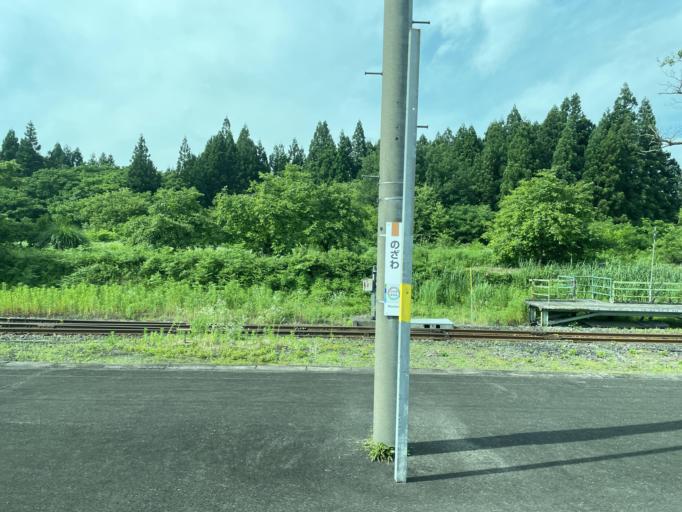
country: JP
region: Fukushima
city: Kitakata
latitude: 37.5912
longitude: 139.6440
